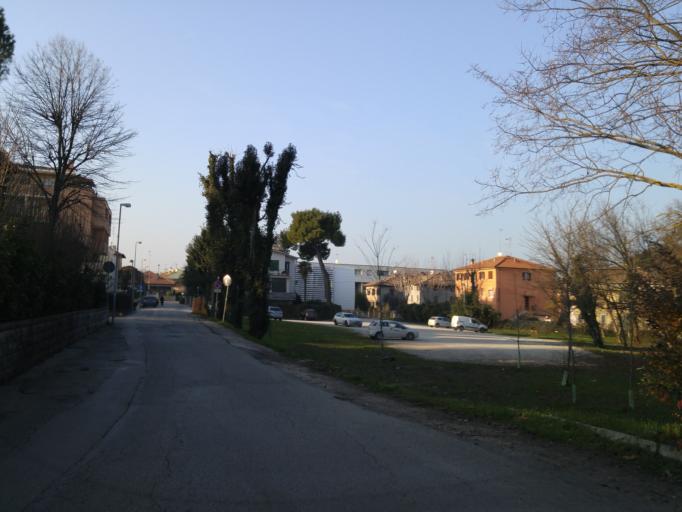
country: IT
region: The Marches
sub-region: Provincia di Pesaro e Urbino
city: Fano
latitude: 43.8390
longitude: 13.0123
